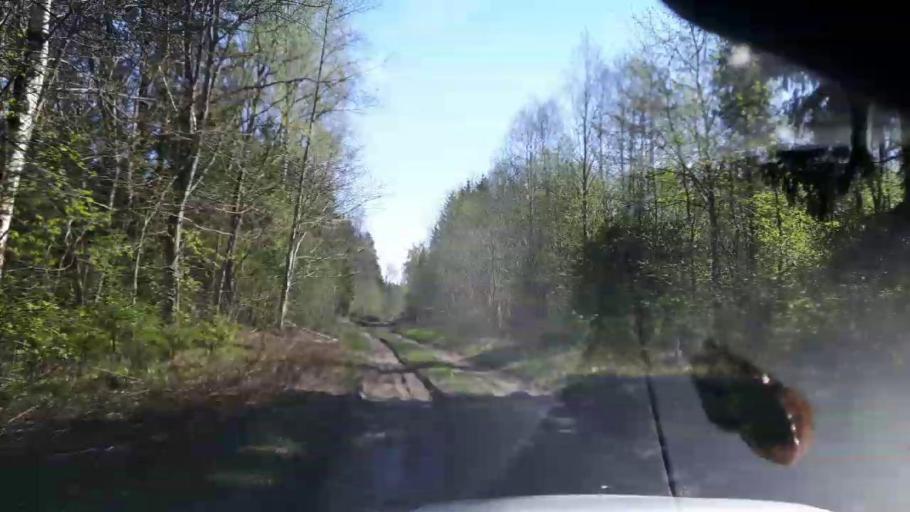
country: EE
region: Paernumaa
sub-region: Tootsi vald
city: Tootsi
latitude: 58.5460
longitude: 24.8013
